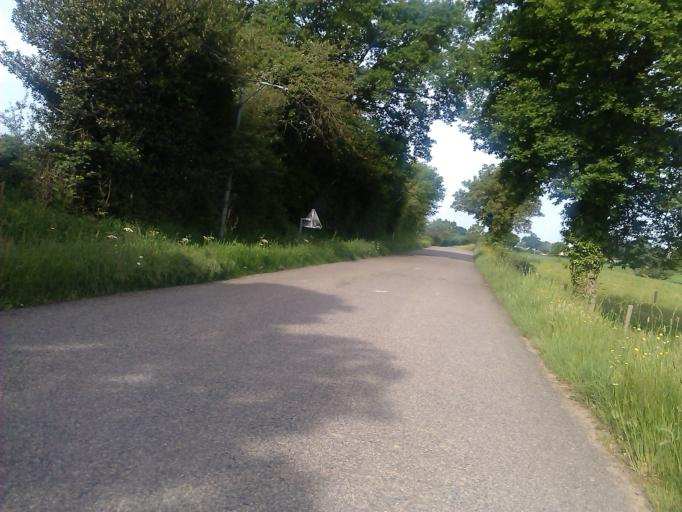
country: FR
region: Auvergne
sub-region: Departement de l'Allier
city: Cerilly
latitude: 46.6152
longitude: 2.7950
